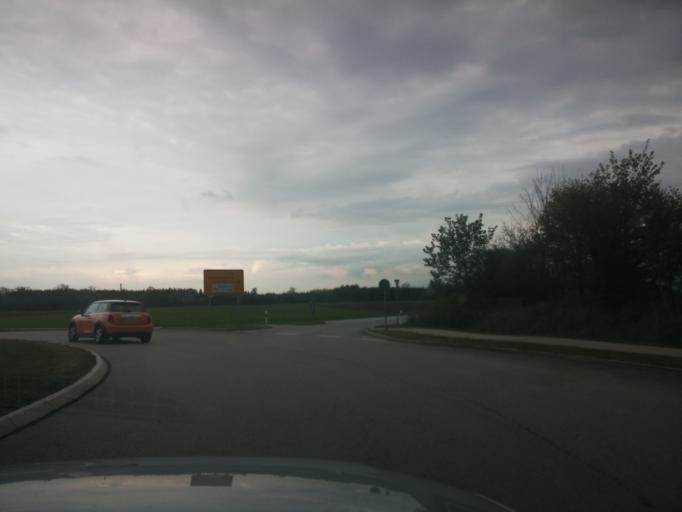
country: DE
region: Bavaria
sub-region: Upper Bavaria
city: Putzbrunn
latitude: 48.0835
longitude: 11.7184
